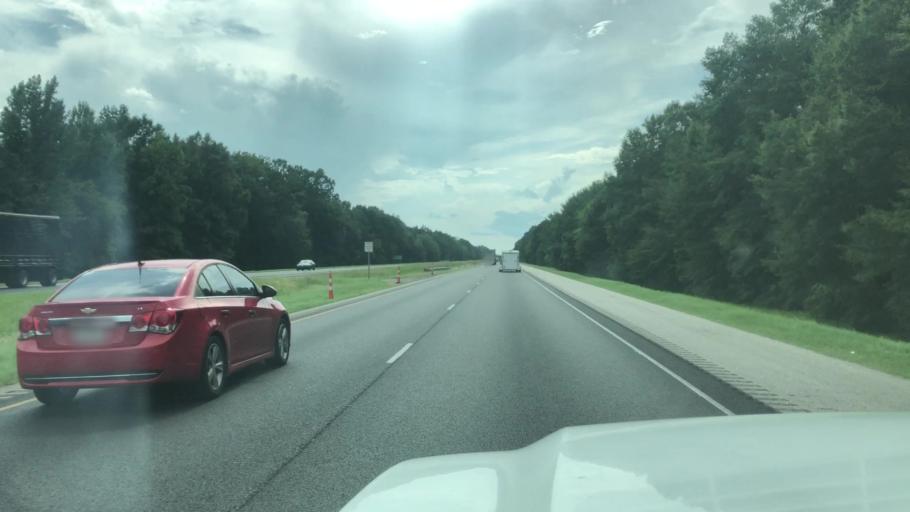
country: US
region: Alabama
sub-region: Montgomery County
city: Pike Road
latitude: 32.3794
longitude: -86.0166
